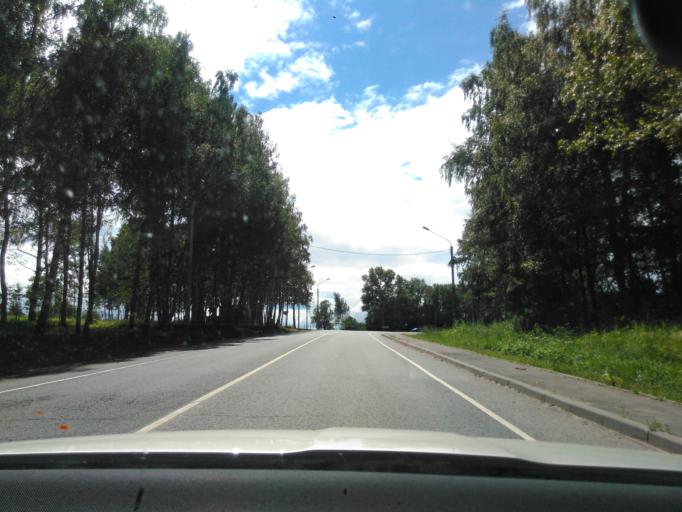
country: RU
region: Moskovskaya
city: Shevlyakovo
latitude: 56.3847
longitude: 36.8586
